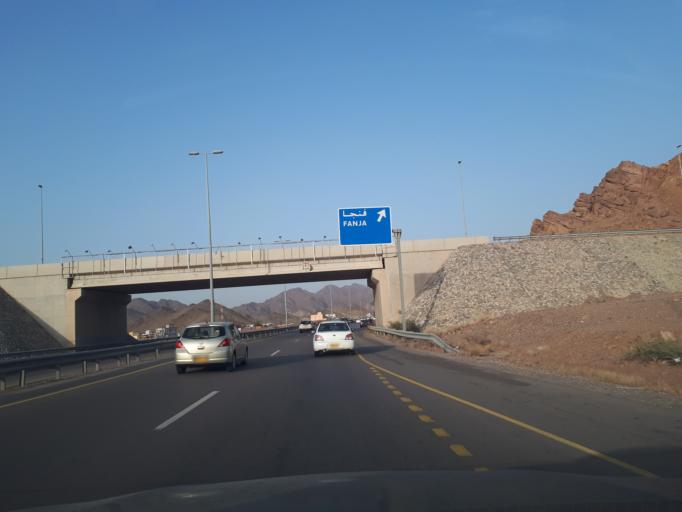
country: OM
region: Muhafazat ad Dakhiliyah
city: Bidbid
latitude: 23.4654
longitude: 58.1263
